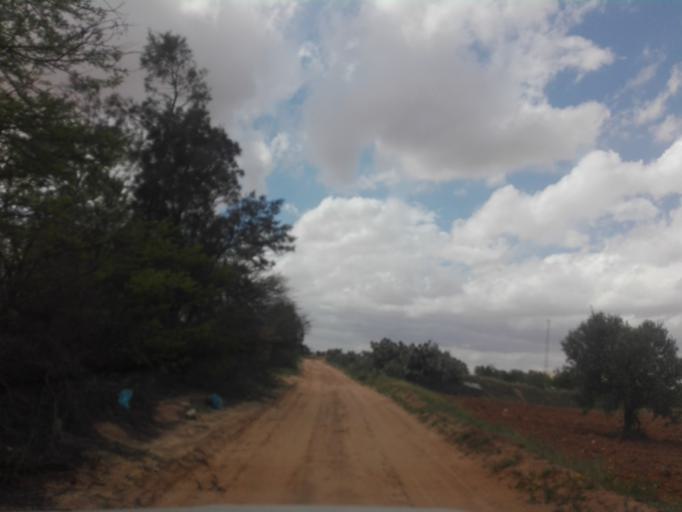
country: TN
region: Safaqis
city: Sfax
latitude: 34.6953
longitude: 10.4461
